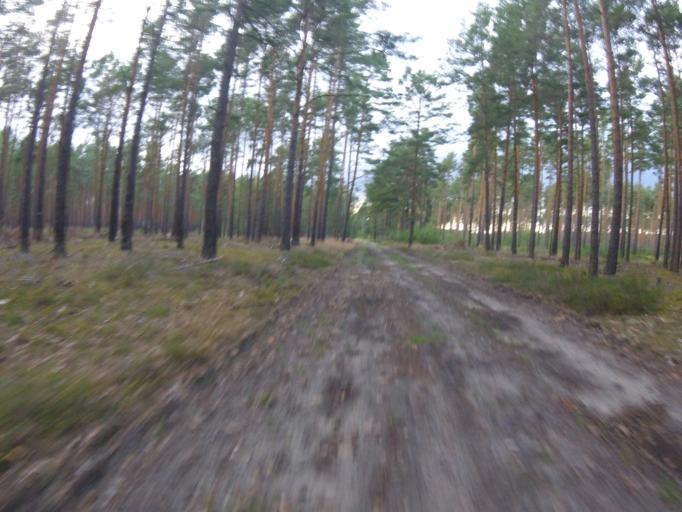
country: DE
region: Brandenburg
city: Gross Koris
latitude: 52.2095
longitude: 13.6749
